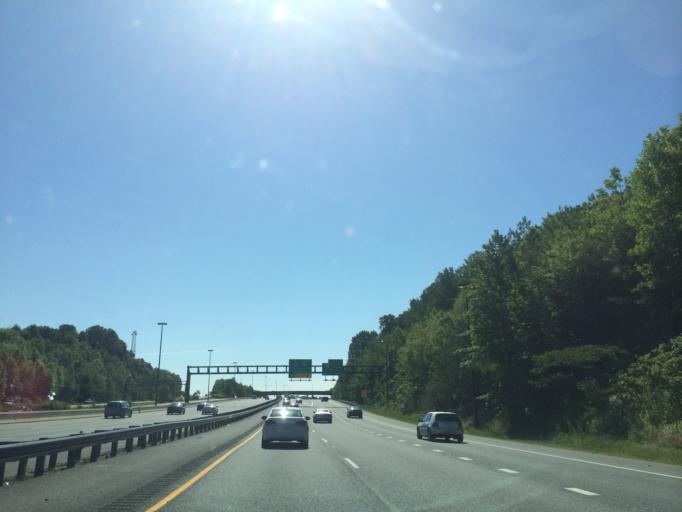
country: US
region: Maryland
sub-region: Anne Arundel County
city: Edgewater
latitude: 38.9836
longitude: -76.5671
